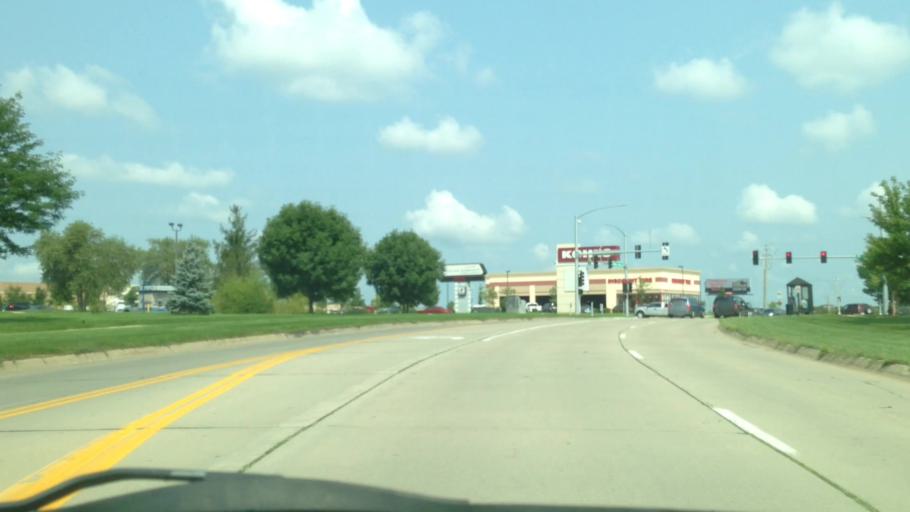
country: US
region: Iowa
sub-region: Linn County
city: Fairfax
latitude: 41.9464
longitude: -91.7207
